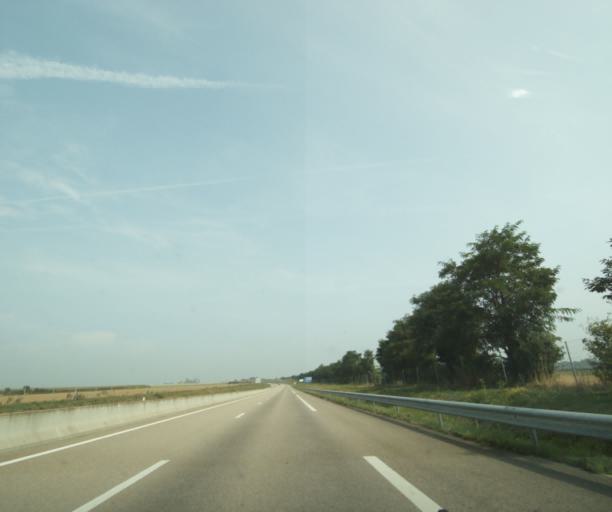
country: FR
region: Lower Normandy
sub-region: Departement de l'Orne
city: Courteilles
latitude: 48.8014
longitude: -0.1260
